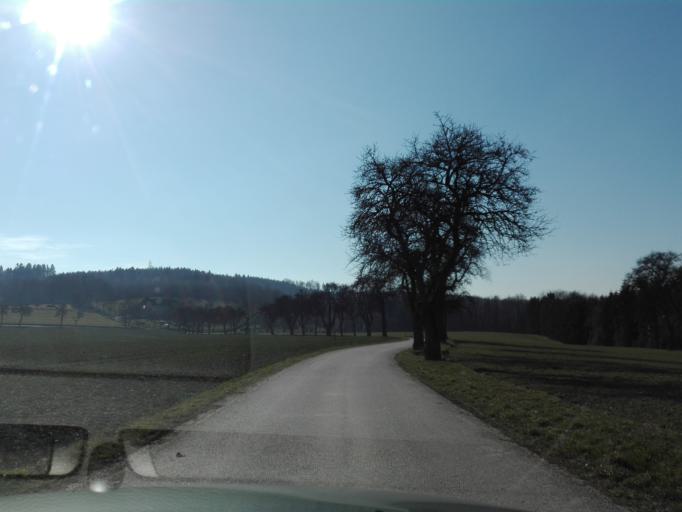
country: AT
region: Upper Austria
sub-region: Wels-Land
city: Holzhausen
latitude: 48.2547
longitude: 14.0880
